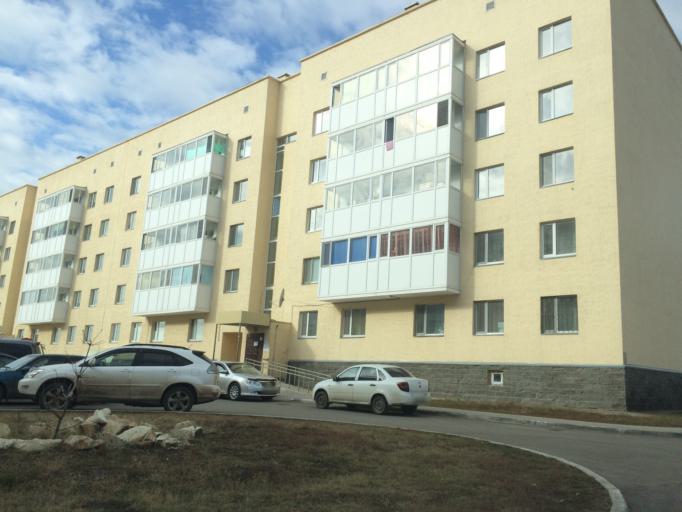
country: KZ
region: Astana Qalasy
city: Astana
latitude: 51.1705
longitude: 71.3715
